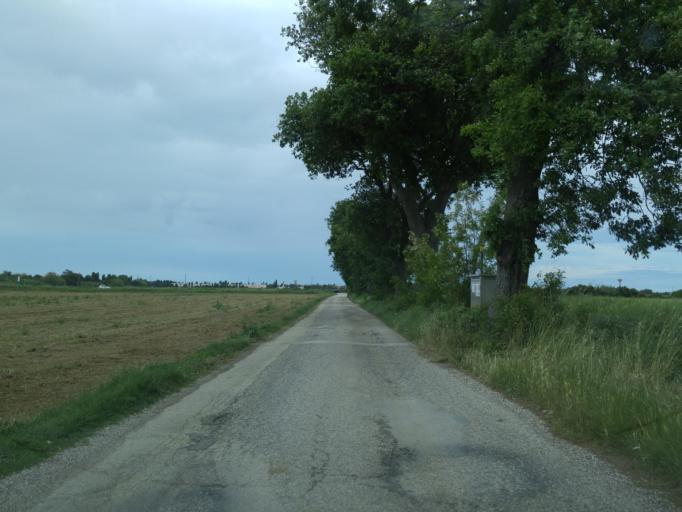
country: IT
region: The Marches
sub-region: Provincia di Pesaro e Urbino
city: Rosciano
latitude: 43.8163
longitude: 13.0199
